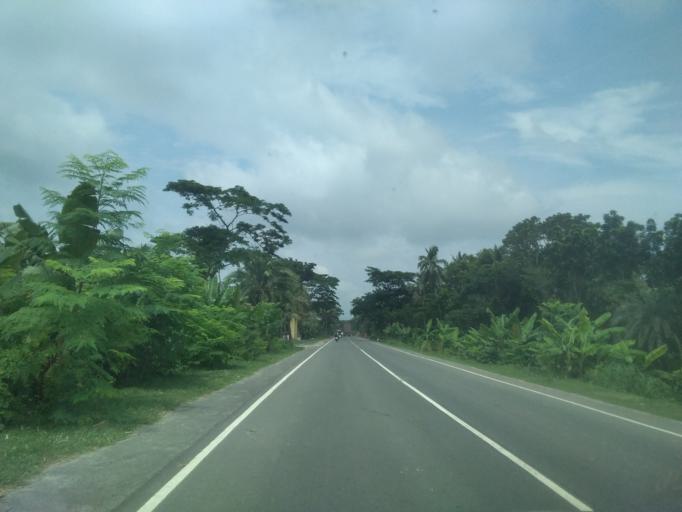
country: BD
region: Khulna
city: Kesabpur
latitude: 22.8168
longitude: 89.2582
